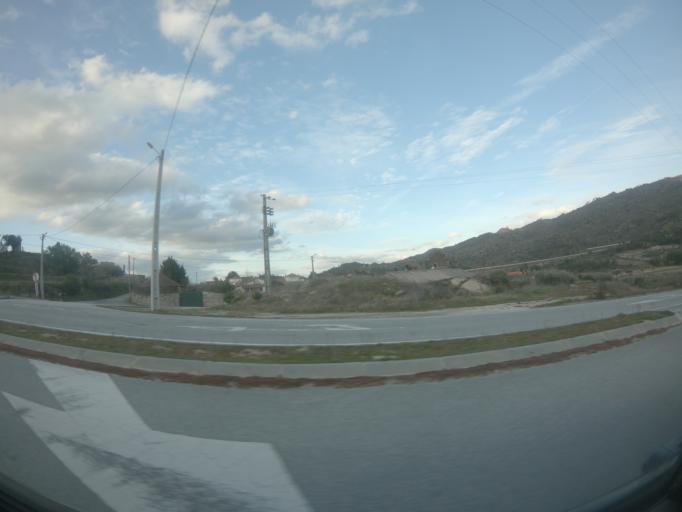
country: PT
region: Braganca
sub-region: Carrazeda de Ansiaes
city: Carrazeda de Anciaes
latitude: 41.2955
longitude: -7.3447
